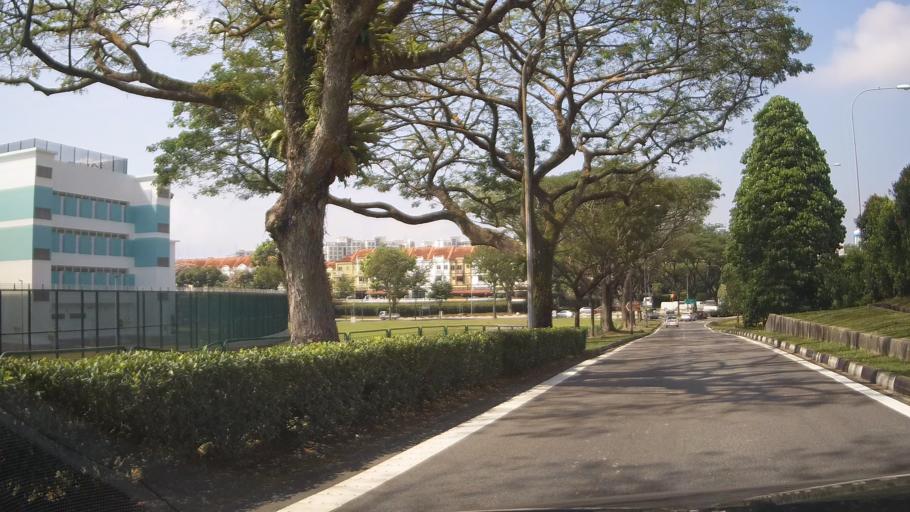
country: MY
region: Johor
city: Johor Bahru
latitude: 1.3563
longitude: 103.6992
